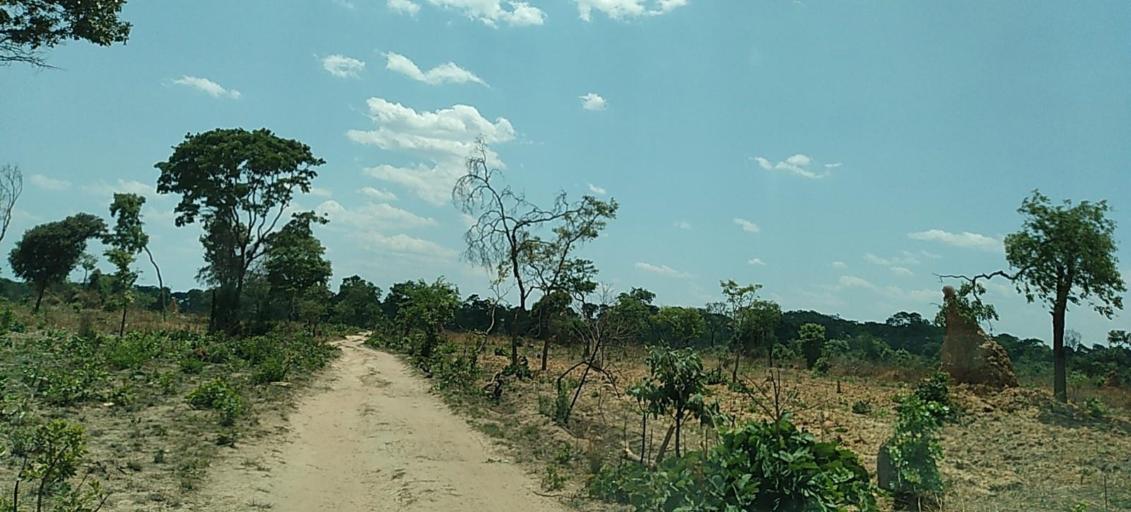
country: ZM
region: Central
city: Kapiri Mposhi
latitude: -13.6341
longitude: 28.7529
